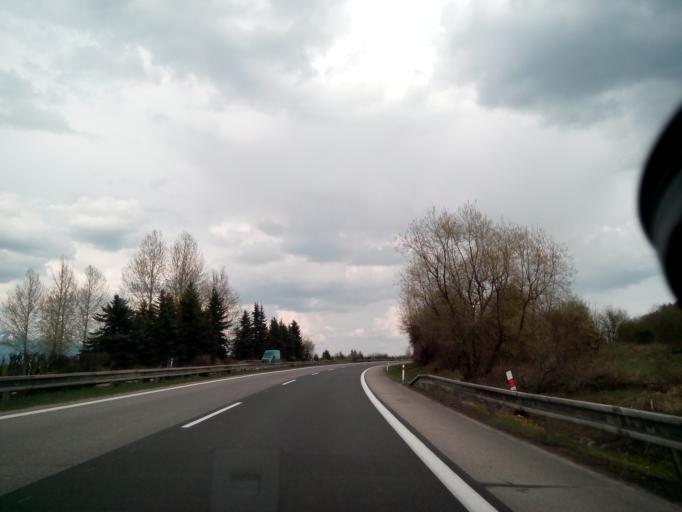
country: SK
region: Zilinsky
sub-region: Okres Liptovsky Mikulas
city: Liptovsky Mikulas
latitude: 49.0904
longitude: 19.4852
